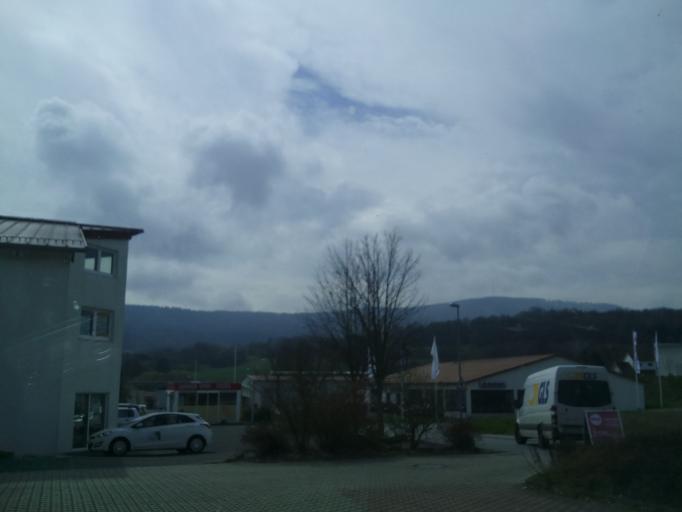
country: DE
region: Bavaria
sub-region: Regierungsbezirk Unterfranken
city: Bischofsheim an der Rhon
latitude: 50.4014
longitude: 10.0173
